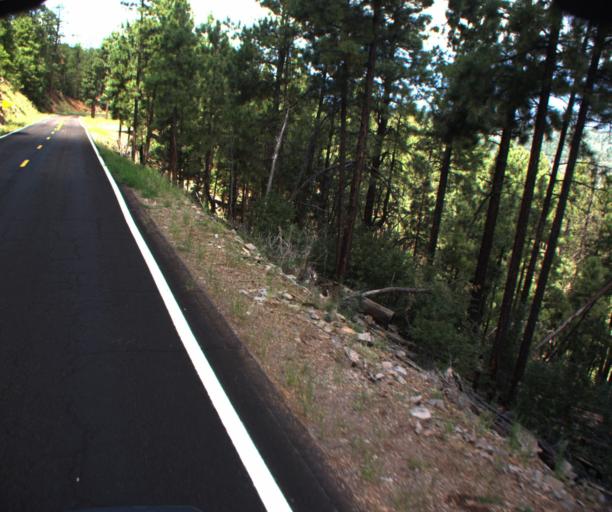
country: US
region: Arizona
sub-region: Greenlee County
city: Morenci
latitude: 33.4668
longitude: -109.3614
